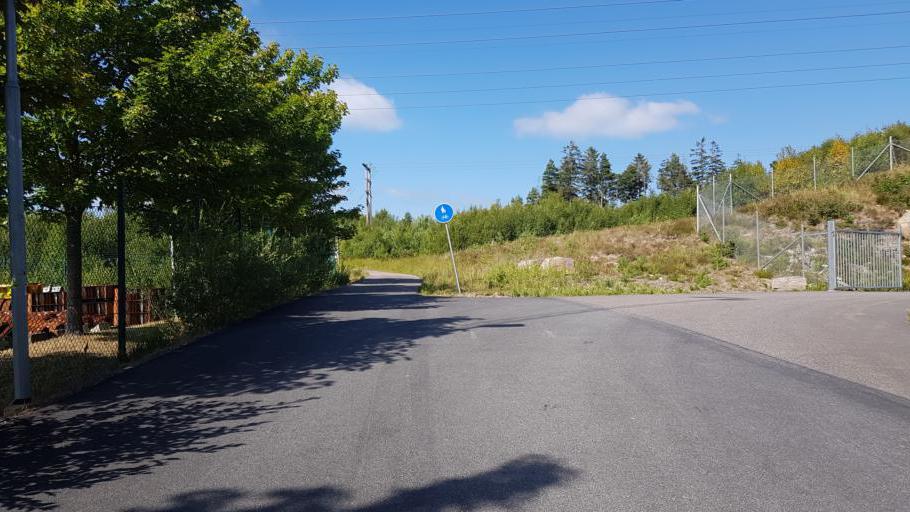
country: SE
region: Vaestra Goetaland
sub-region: Harryda Kommun
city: Molnlycke
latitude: 57.6768
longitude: 12.0901
